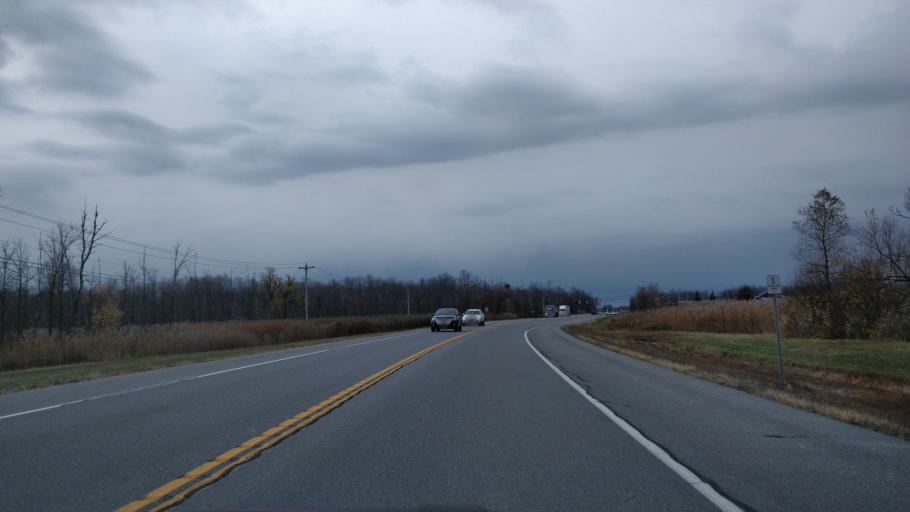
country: US
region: New York
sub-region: St. Lawrence County
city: Ogdensburg
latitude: 44.7077
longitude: -75.4532
